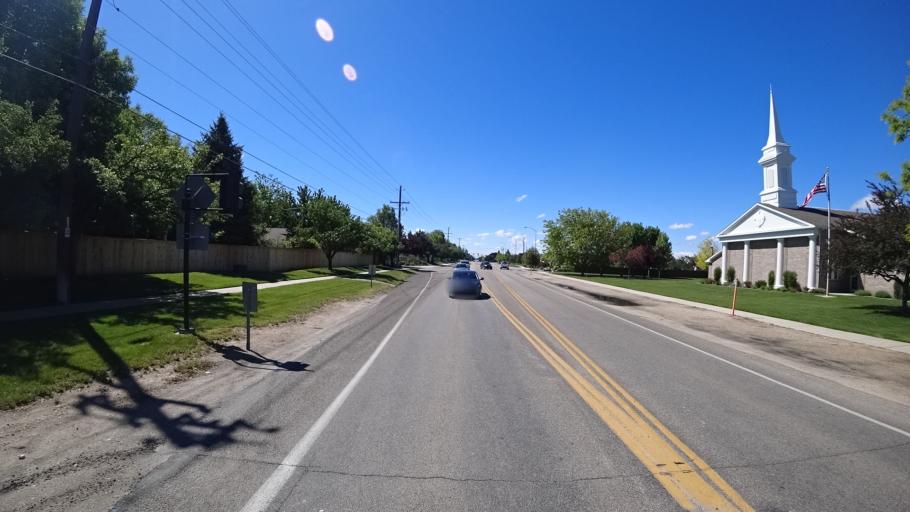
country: US
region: Idaho
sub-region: Ada County
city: Meridian
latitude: 43.6366
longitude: -116.3745
